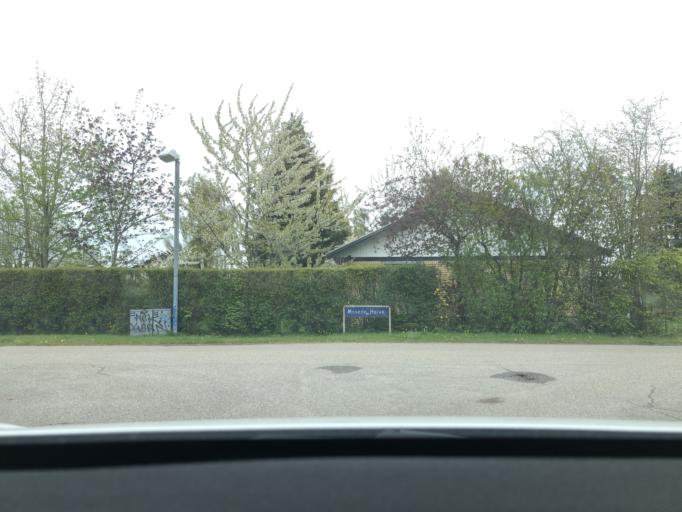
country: DK
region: Zealand
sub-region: Greve Kommune
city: Greve
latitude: 55.5714
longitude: 12.2722
